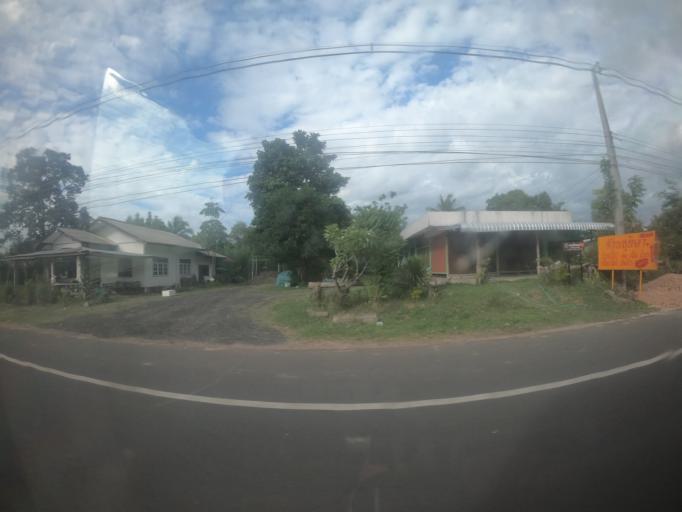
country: TH
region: Surin
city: Prasat
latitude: 14.6111
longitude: 103.4192
